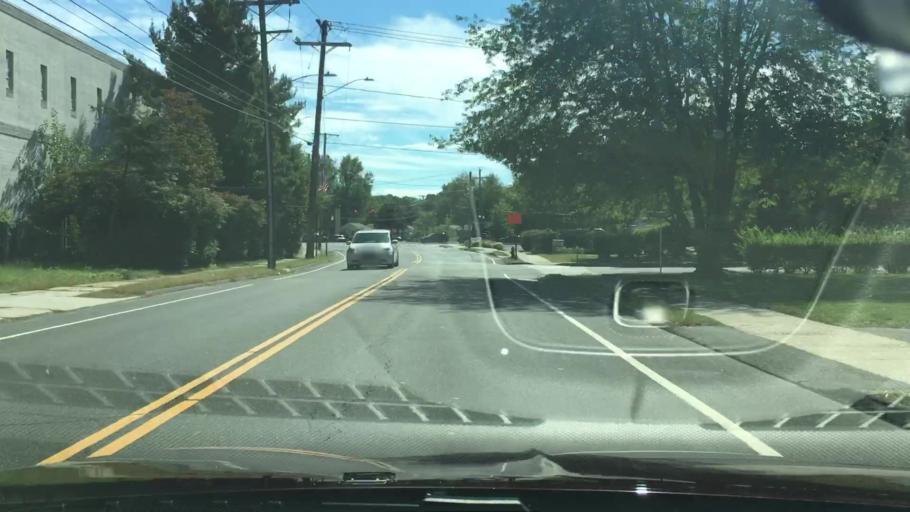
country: US
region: Connecticut
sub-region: Hartford County
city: Bristol
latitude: 41.6945
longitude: -72.9157
